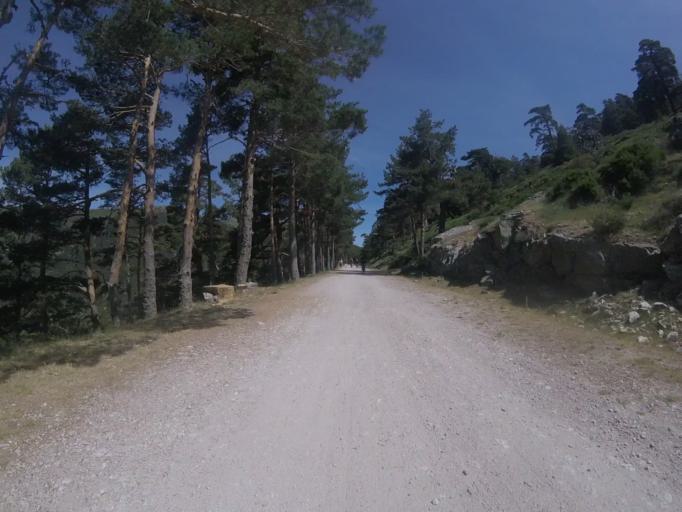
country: ES
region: Madrid
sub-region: Provincia de Madrid
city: Cercedilla
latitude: 40.7866
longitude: -4.0587
